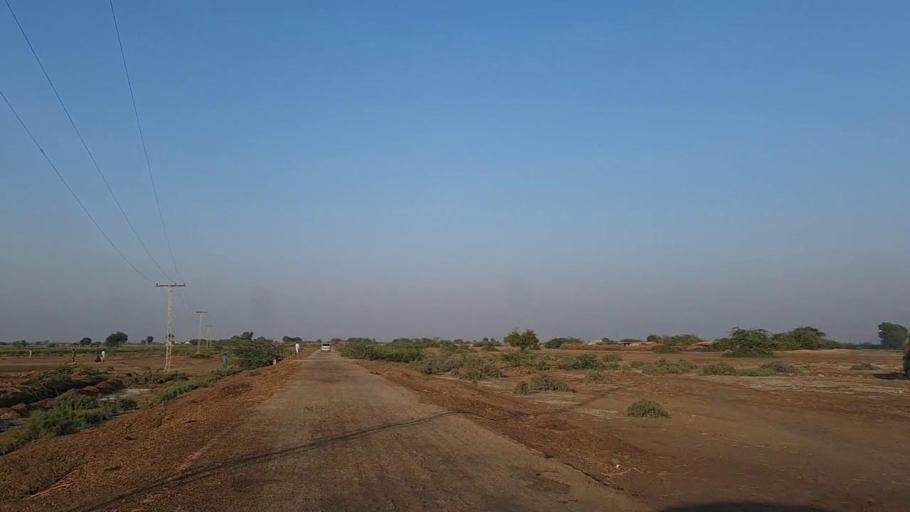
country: PK
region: Sindh
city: Naukot
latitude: 24.9496
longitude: 69.4476
